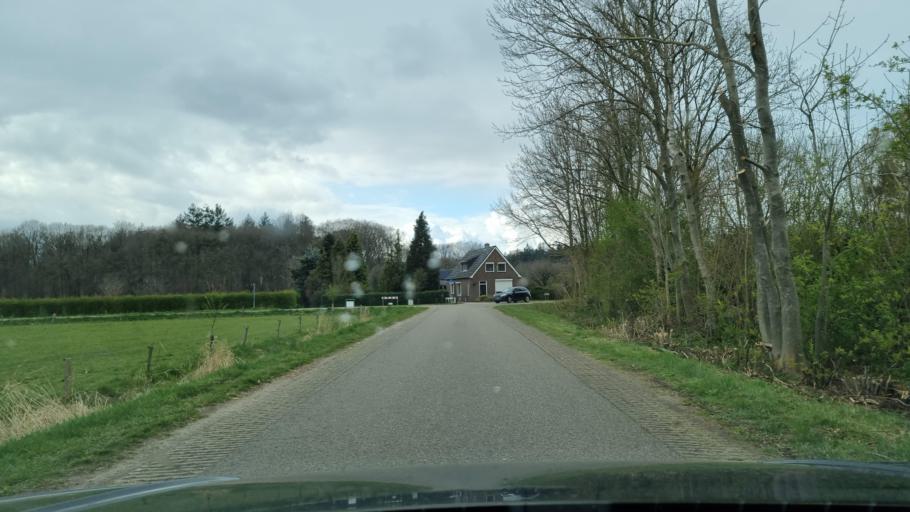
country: NL
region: Gelderland
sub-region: Gemeente Montferland
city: s-Heerenberg
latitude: 51.9000
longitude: 6.1764
